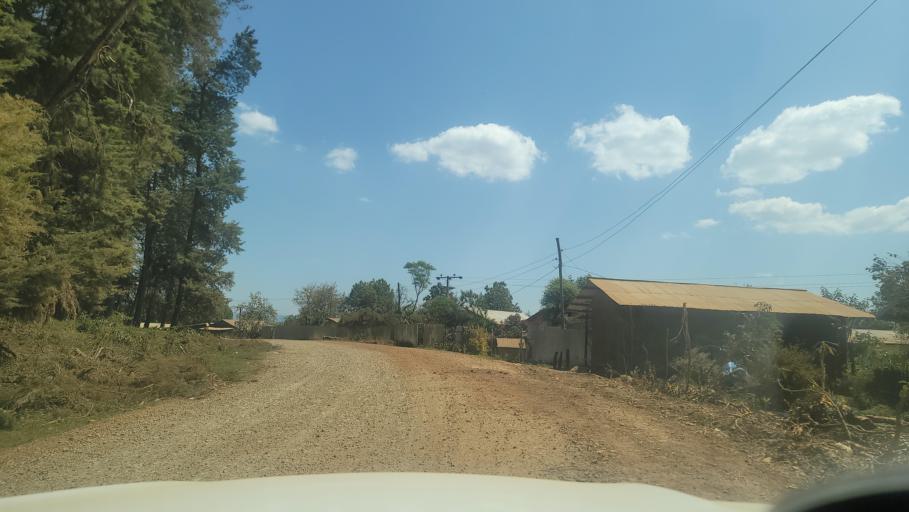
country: ET
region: Oromiya
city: Agaro
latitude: 7.7842
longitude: 36.4103
